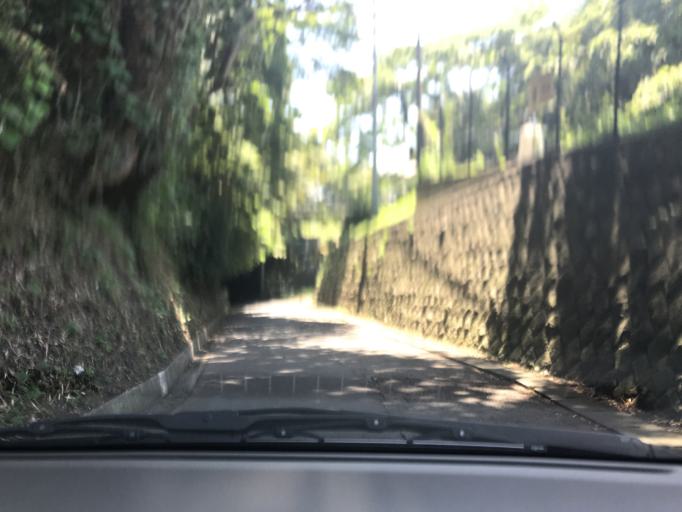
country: JP
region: Kanagawa
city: Fujisawa
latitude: 35.3495
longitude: 139.4411
